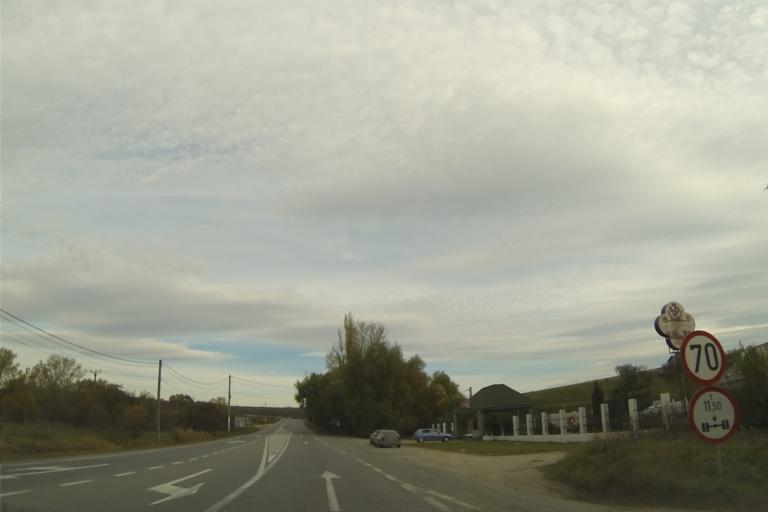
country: RO
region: Olt
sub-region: Comuna Valea Mare
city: Valea Mare
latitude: 44.4818
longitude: 24.4383
